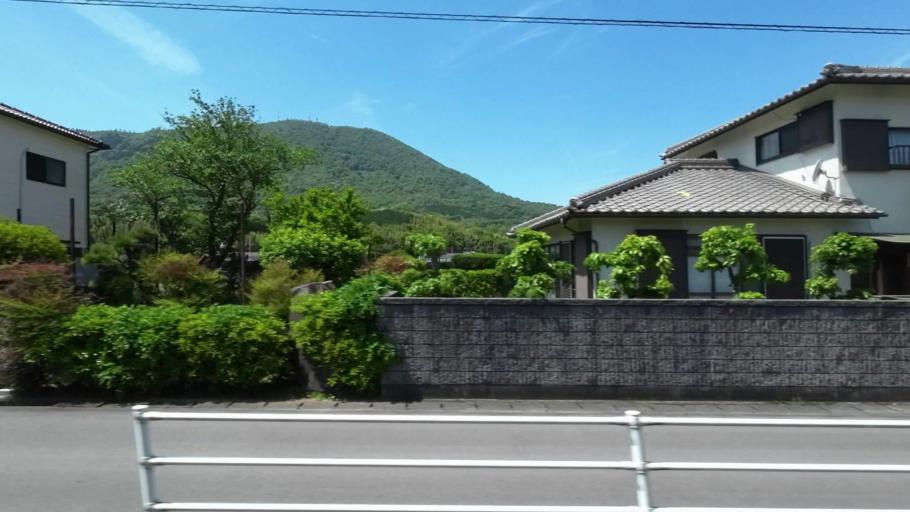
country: JP
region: Kagawa
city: Marugame
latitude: 34.2127
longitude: 133.8018
